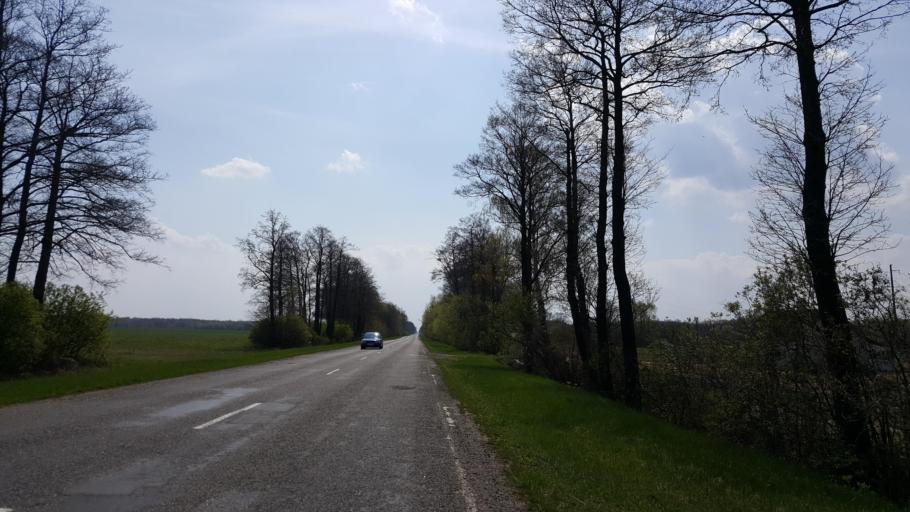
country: BY
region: Brest
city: Zhabinka
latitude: 52.2949
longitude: 23.9381
